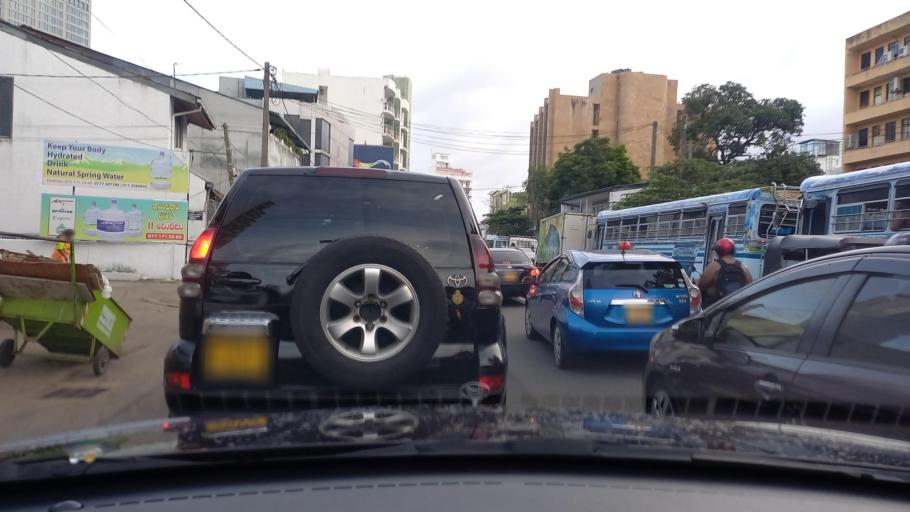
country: LK
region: Western
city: Pita Kotte
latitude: 6.8804
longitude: 79.8696
